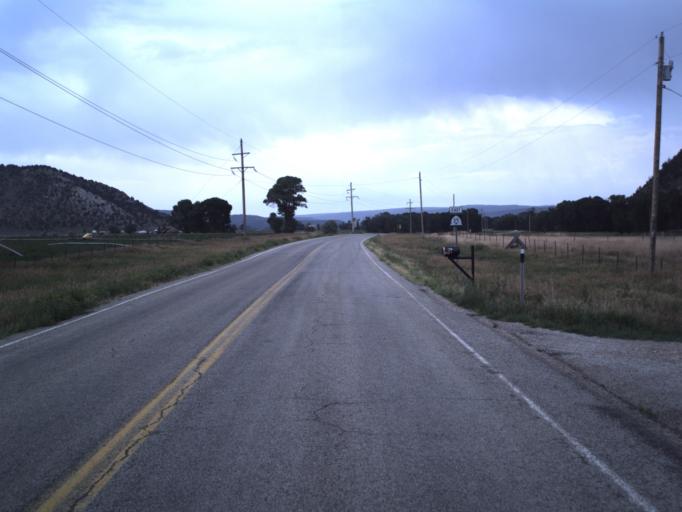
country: US
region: Utah
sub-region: Duchesne County
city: Duchesne
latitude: 40.3989
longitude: -110.7581
